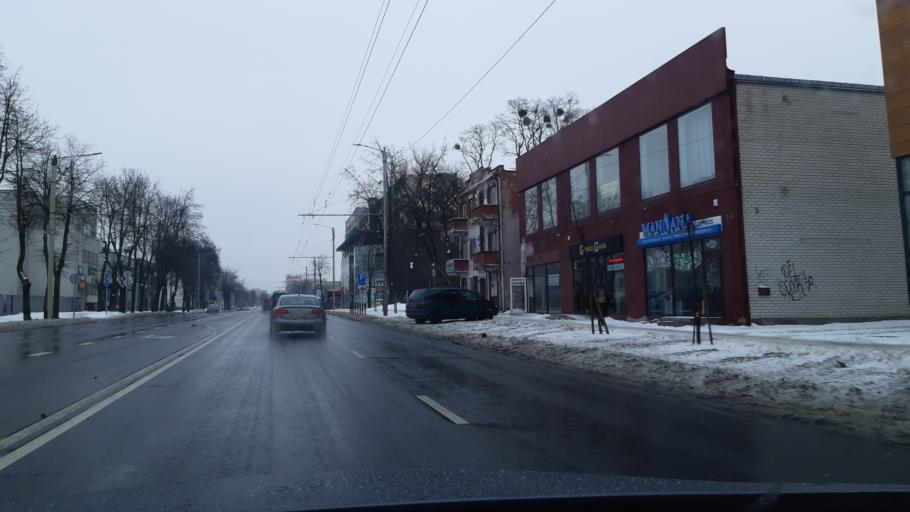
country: LT
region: Kauno apskritis
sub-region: Kaunas
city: Kaunas
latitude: 54.9066
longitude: 23.9232
